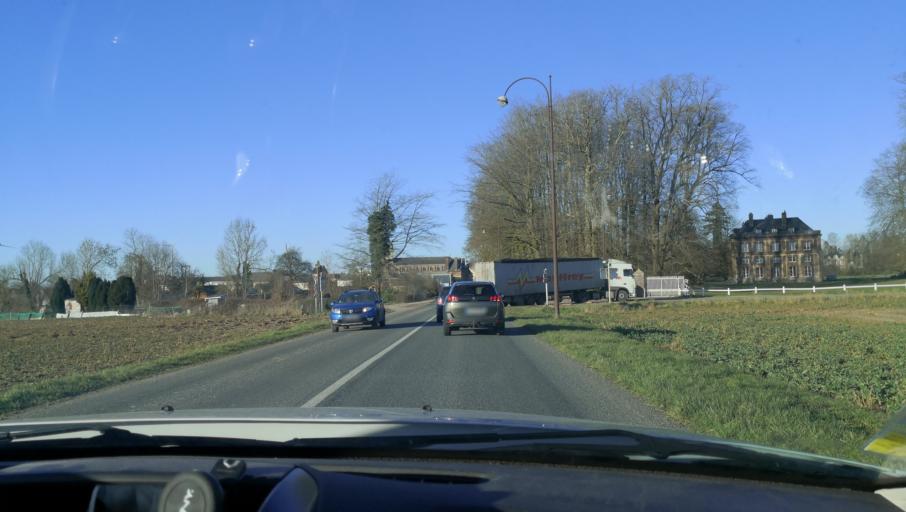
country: FR
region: Haute-Normandie
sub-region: Departement de la Seine-Maritime
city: Totes
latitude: 49.6751
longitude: 1.0449
